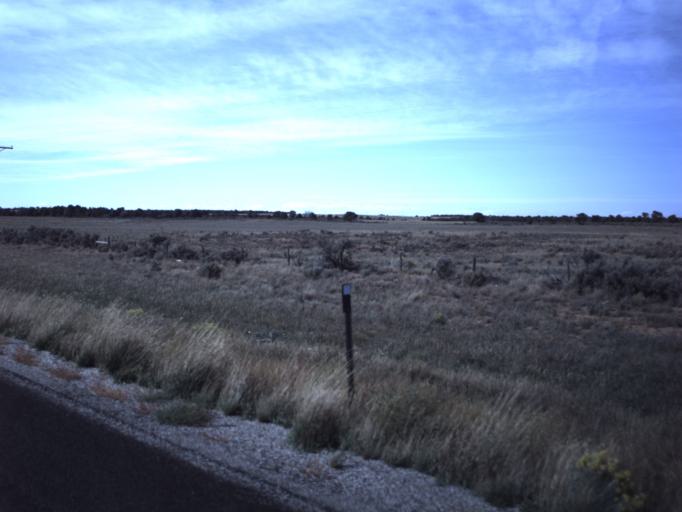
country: US
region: Utah
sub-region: San Juan County
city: Monticello
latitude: 37.8543
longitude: -109.1825
